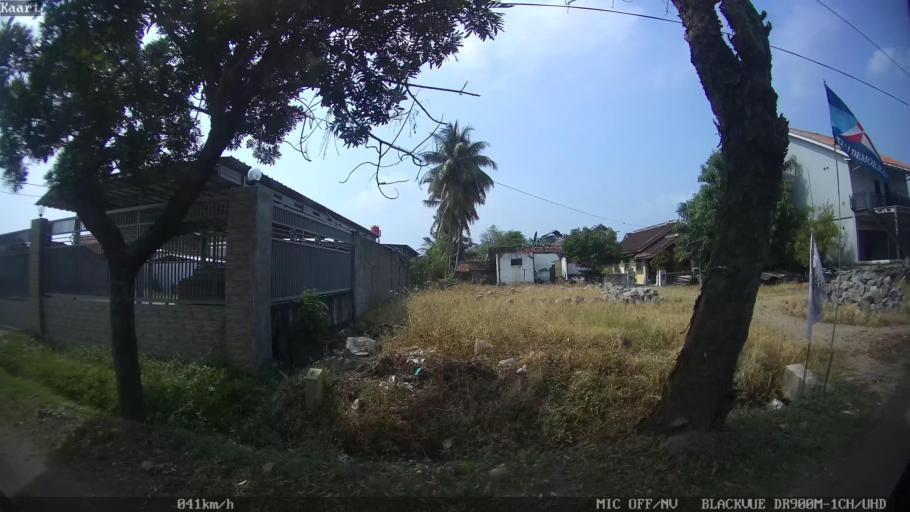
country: ID
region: Lampung
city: Gadingrejo
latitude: -5.3766
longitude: 105.0368
